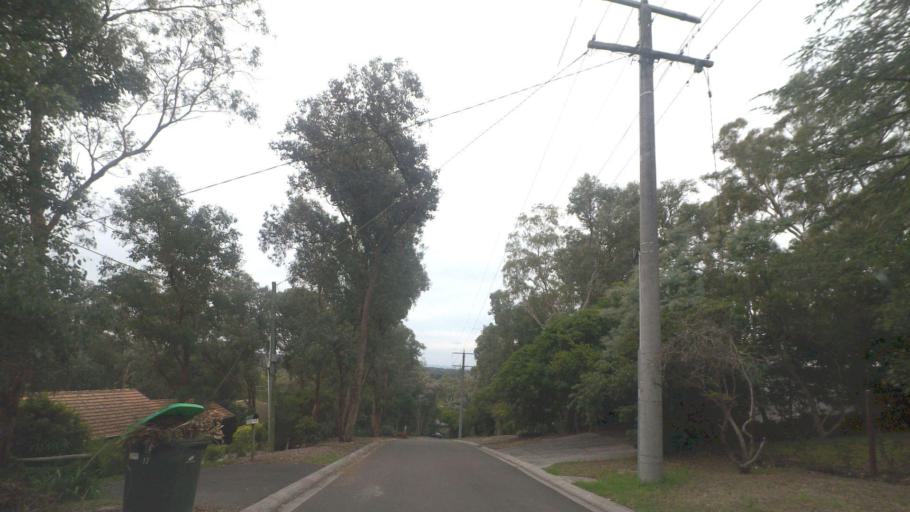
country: AU
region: Victoria
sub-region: Nillumbik
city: North Warrandyte
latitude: -37.7490
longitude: 145.2045
